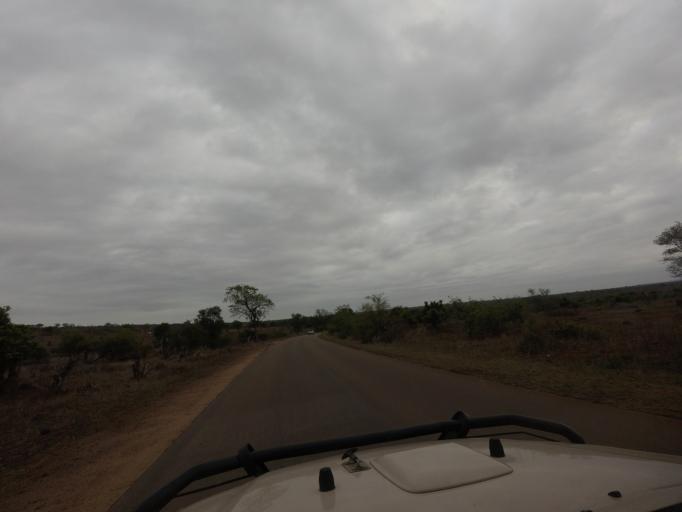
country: ZA
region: Mpumalanga
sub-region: Ehlanzeni District
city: Komatipoort
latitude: -25.3393
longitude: 31.8798
